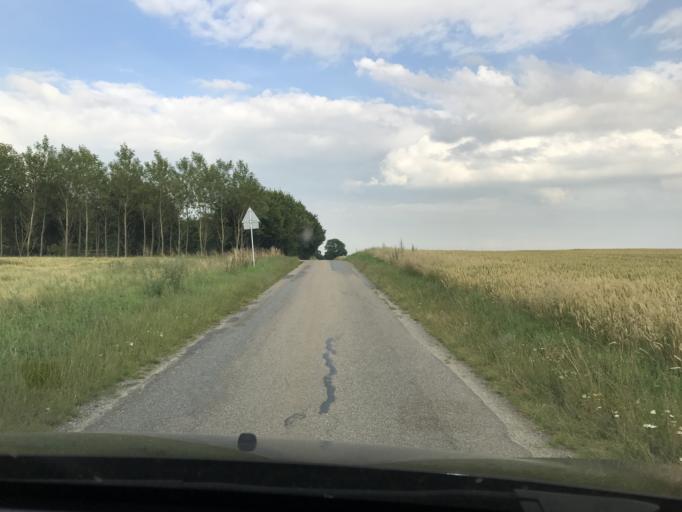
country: DK
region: South Denmark
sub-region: Vejle Kommune
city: Jelling
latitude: 55.8048
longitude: 9.4028
